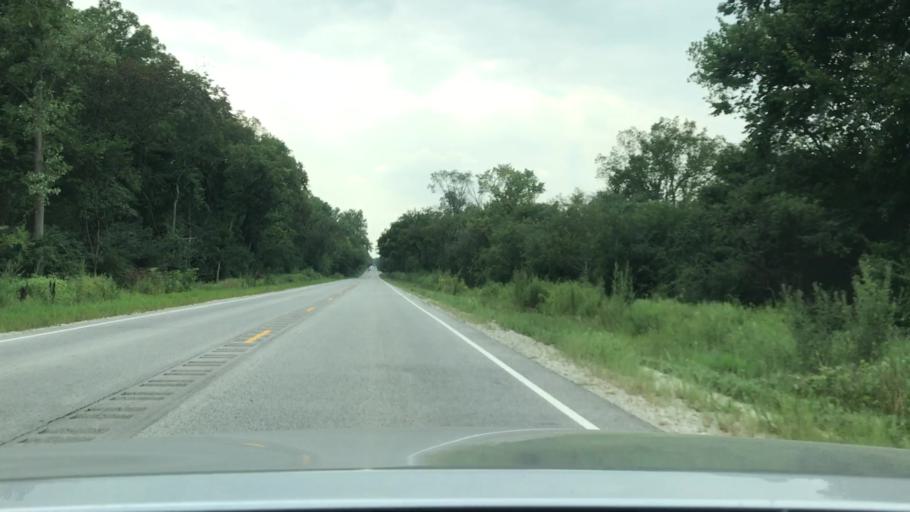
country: US
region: Illinois
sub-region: DuPage County
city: Burr Ridge
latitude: 41.6877
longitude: -87.9055
